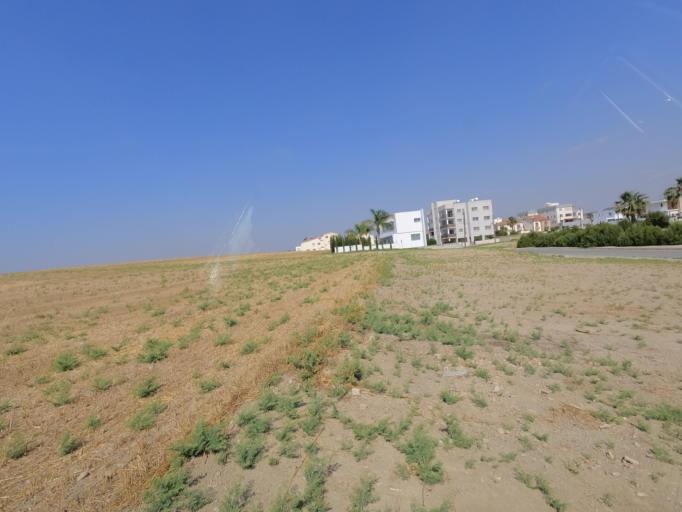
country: CY
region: Larnaka
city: Dhromolaxia
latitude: 34.9025
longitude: 33.5860
